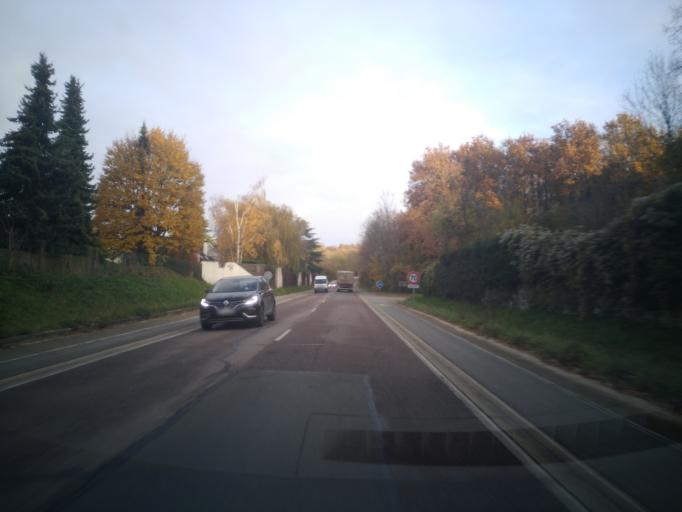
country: FR
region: Ile-de-France
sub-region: Departement des Yvelines
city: Saint-Nom-la-Breteche
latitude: 48.8602
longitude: 2.0310
